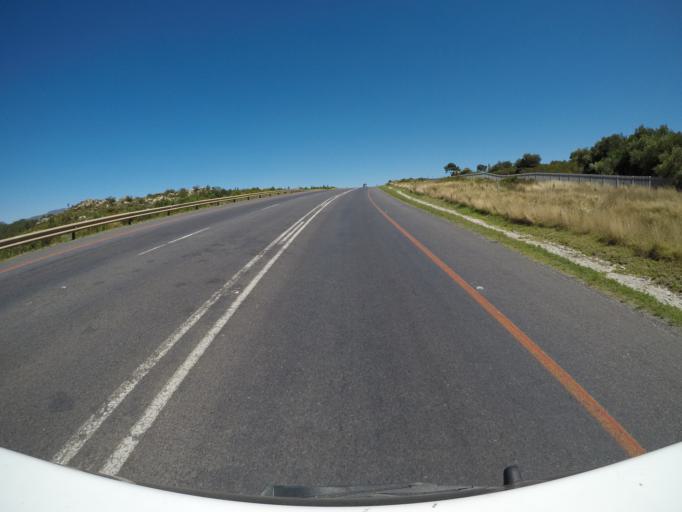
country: ZA
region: Western Cape
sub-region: Overberg District Municipality
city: Grabouw
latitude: -34.1667
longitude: 18.9984
